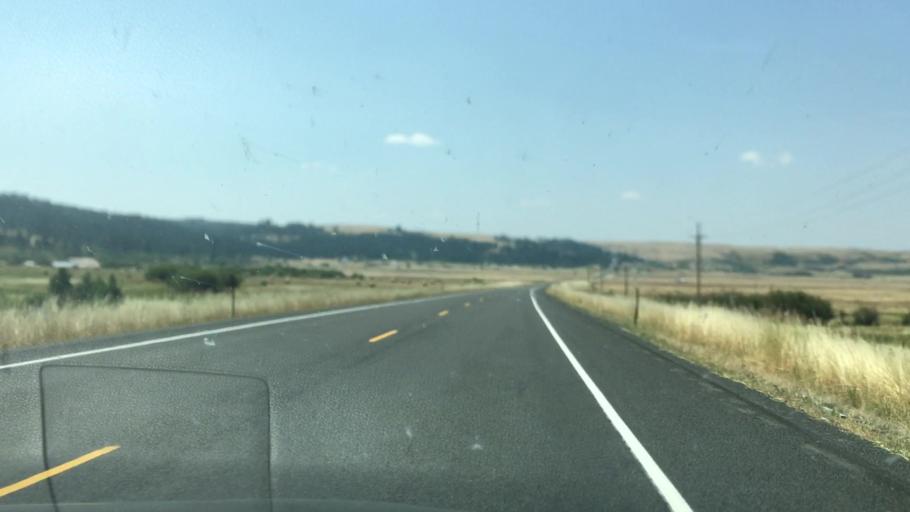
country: US
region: Idaho
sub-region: Idaho County
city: Grangeville
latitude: 45.8938
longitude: -116.1909
